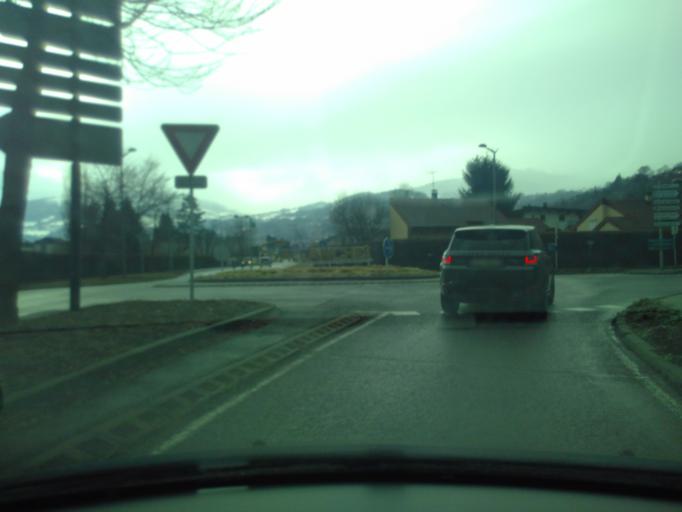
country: FR
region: Rhone-Alpes
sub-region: Departement de la Haute-Savoie
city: Sallanches
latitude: 45.9499
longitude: 6.6298
